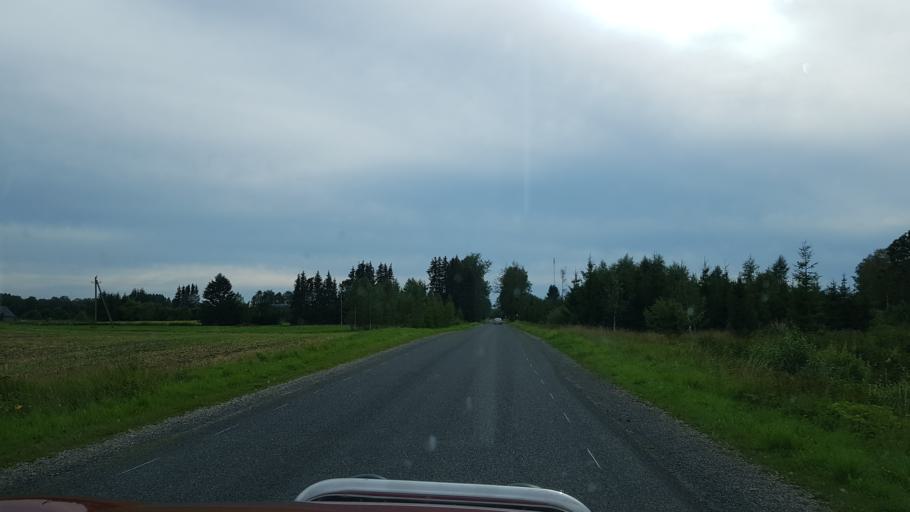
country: EE
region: Laeaene
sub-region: Lihula vald
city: Lihula
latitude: 58.8911
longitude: 23.8813
